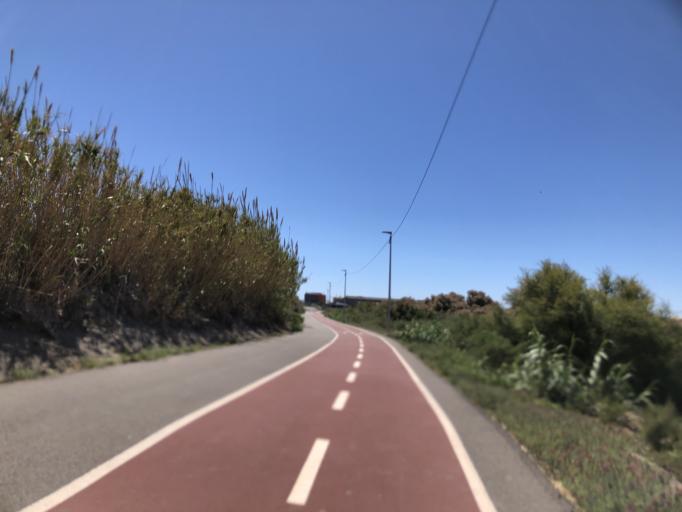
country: ES
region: Andalusia
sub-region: Provincia de Almeria
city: Almeria
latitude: 36.8345
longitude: -2.4034
